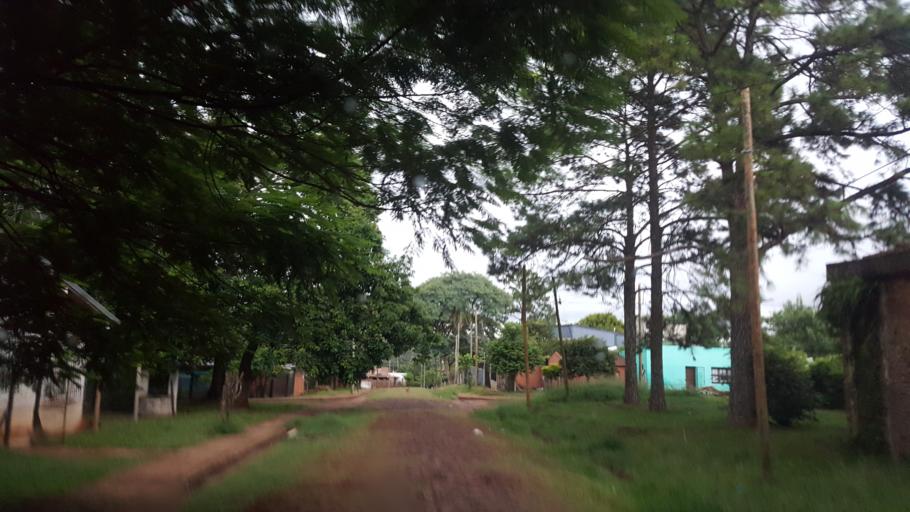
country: AR
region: Misiones
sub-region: Departamento de Capital
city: Posadas
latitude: -27.3983
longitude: -55.9421
